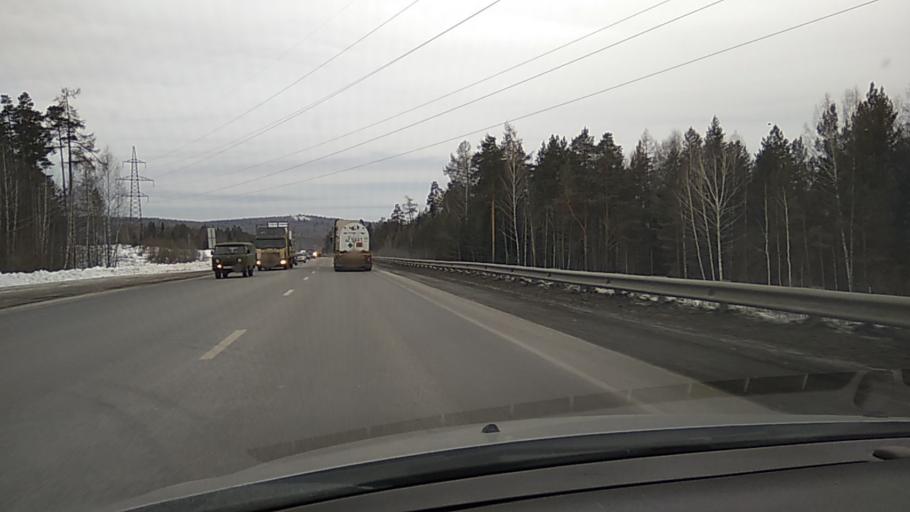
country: RU
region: Sverdlovsk
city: Talitsa
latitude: 56.8486
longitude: 60.0434
